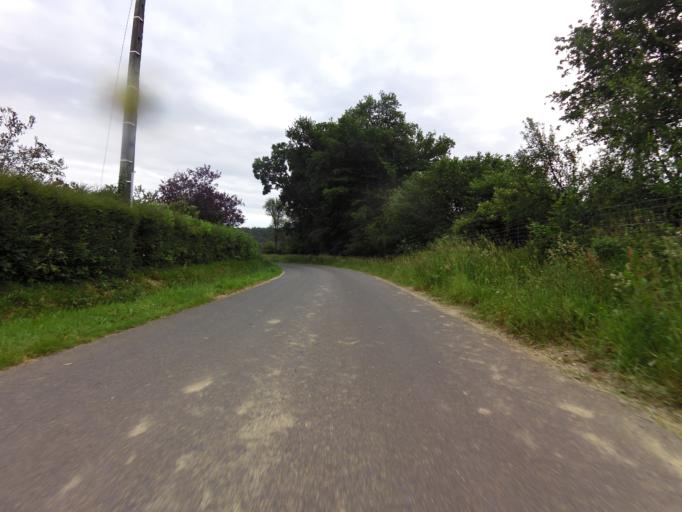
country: FR
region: Brittany
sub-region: Departement du Morbihan
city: Pluherlin
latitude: 47.7154
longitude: -2.3841
